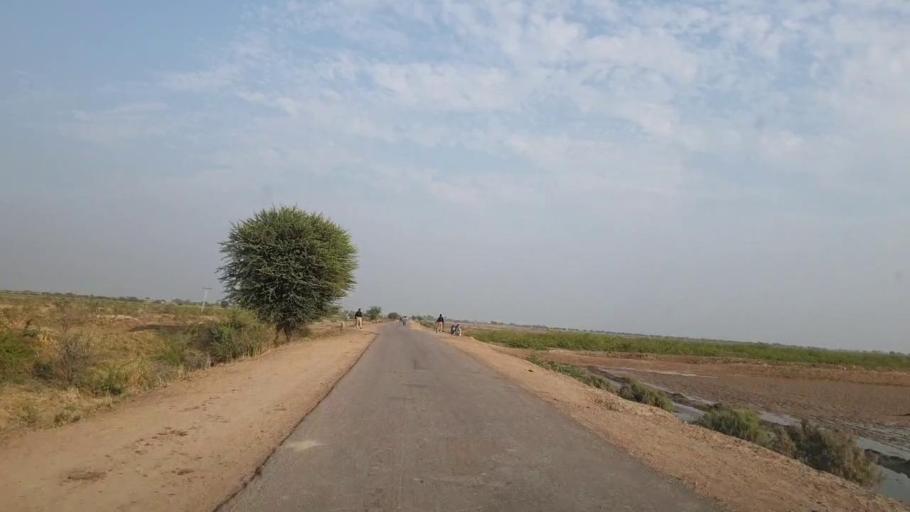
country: PK
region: Sindh
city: Pithoro
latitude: 25.5863
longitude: 69.3356
